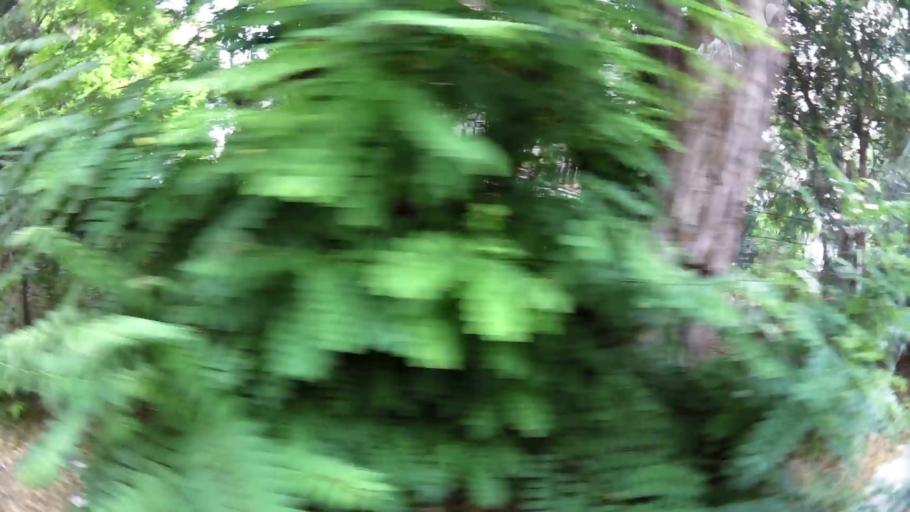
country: GR
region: Central Macedonia
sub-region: Nomos Thessalonikis
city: Thermi
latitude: 40.5456
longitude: 23.0184
